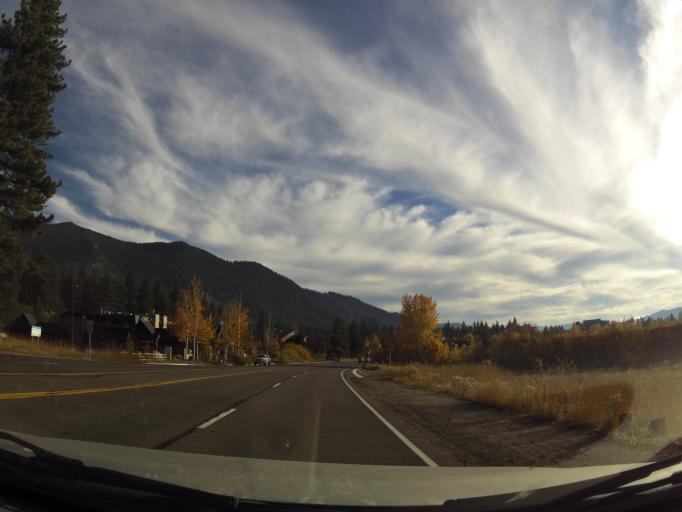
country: US
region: Nevada
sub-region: Douglas County
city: Kingsbury
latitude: 38.9721
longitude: -119.9351
